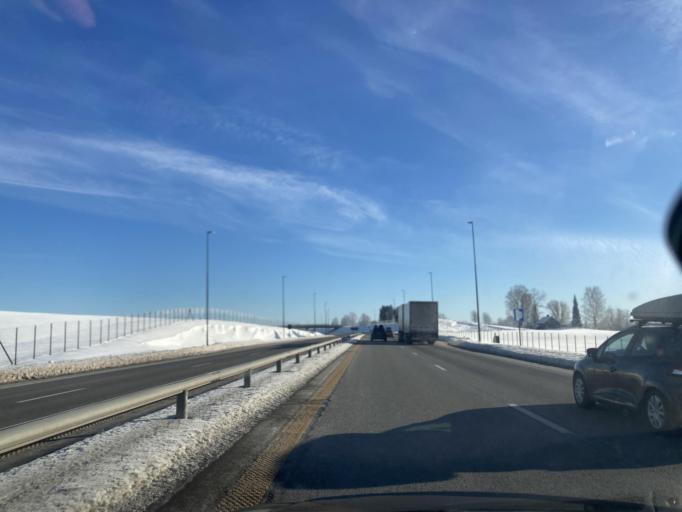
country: NO
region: Hedmark
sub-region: Loten
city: Loten
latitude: 60.8382
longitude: 11.3255
